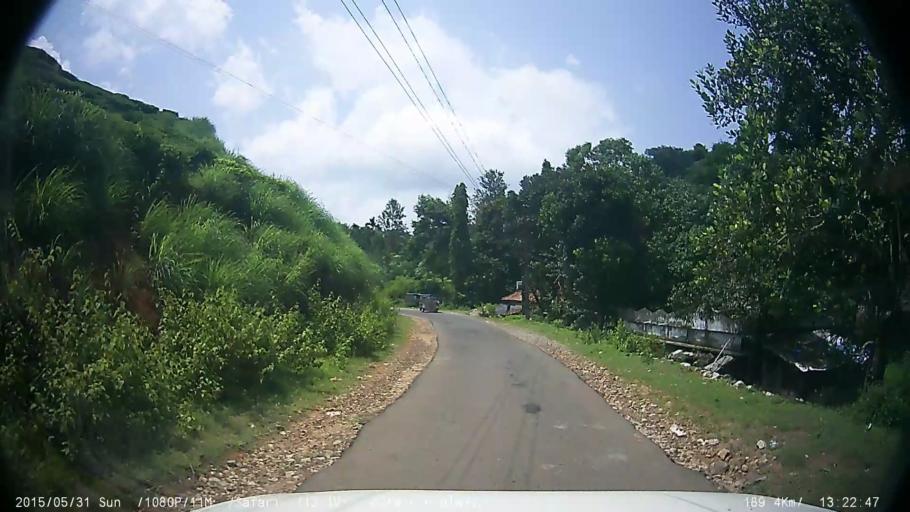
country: IN
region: Kerala
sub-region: Wayanad
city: Kalpetta
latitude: 11.5374
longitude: 76.1353
